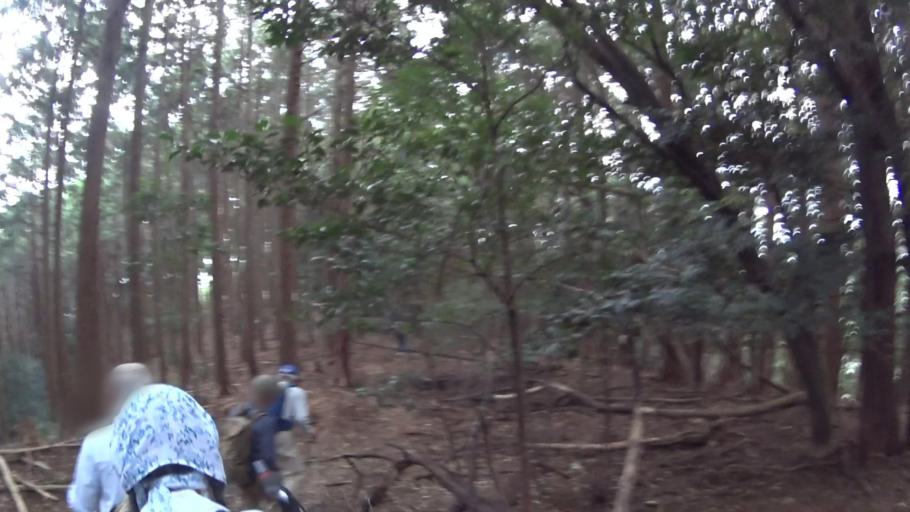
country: JP
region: Osaka
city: Kaizuka
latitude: 34.4899
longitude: 135.3225
